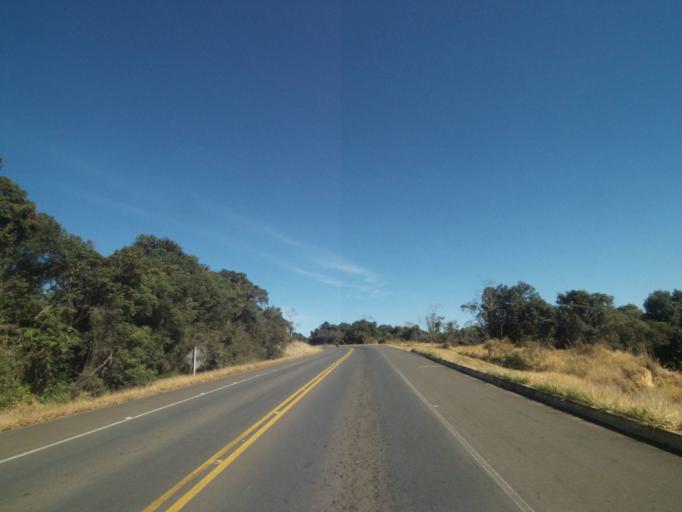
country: BR
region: Parana
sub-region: Tibagi
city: Tibagi
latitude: -24.7544
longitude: -50.4677
